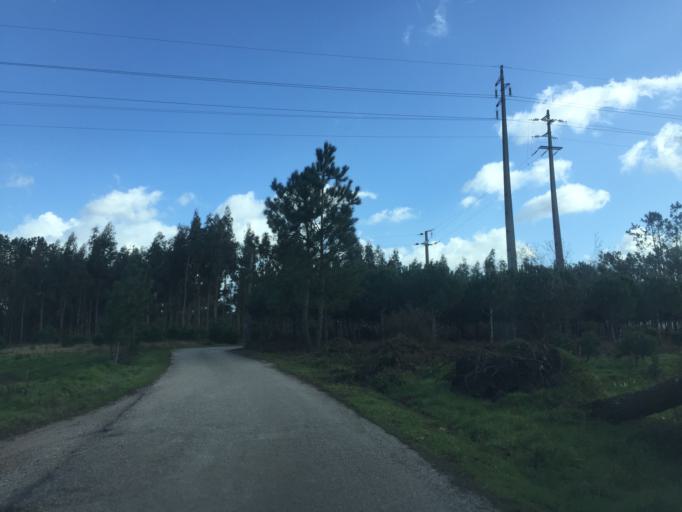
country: PT
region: Coimbra
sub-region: Figueira da Foz
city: Lavos
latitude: 40.0170
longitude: -8.8208
